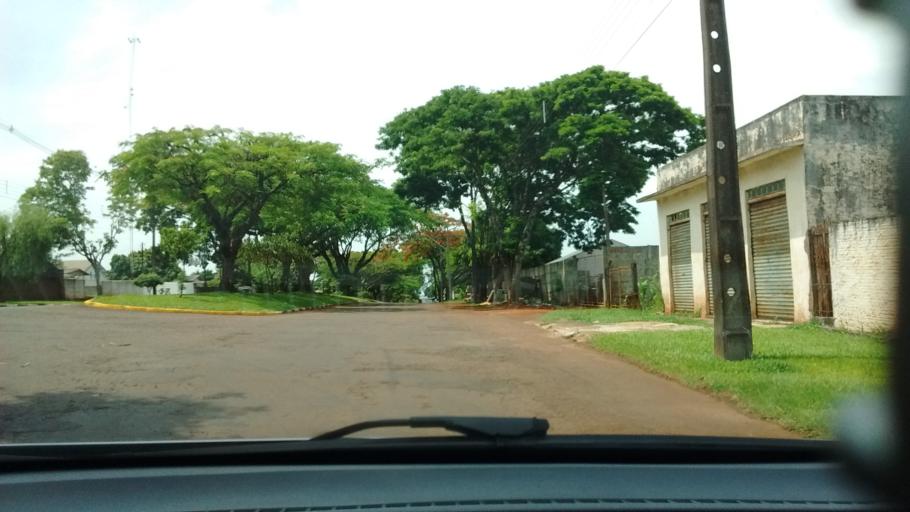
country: BR
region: Parana
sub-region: Corbelia
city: Corbelia
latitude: -24.5449
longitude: -52.9820
